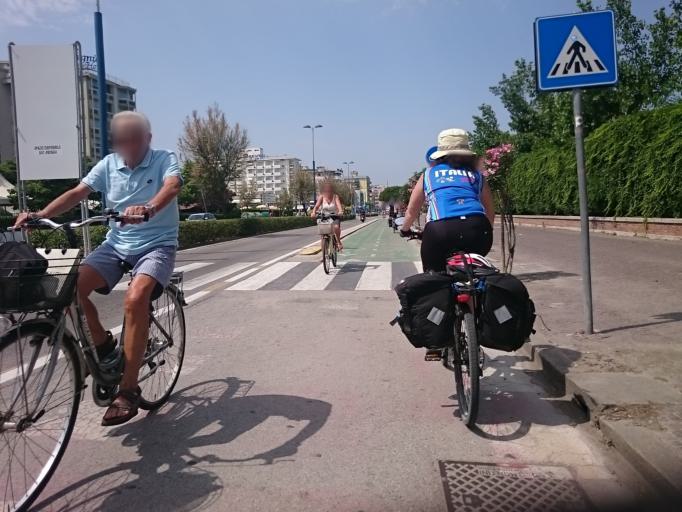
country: IT
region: Veneto
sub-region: Provincia di Venezia
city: Chioggia
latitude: 45.2110
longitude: 12.2956
